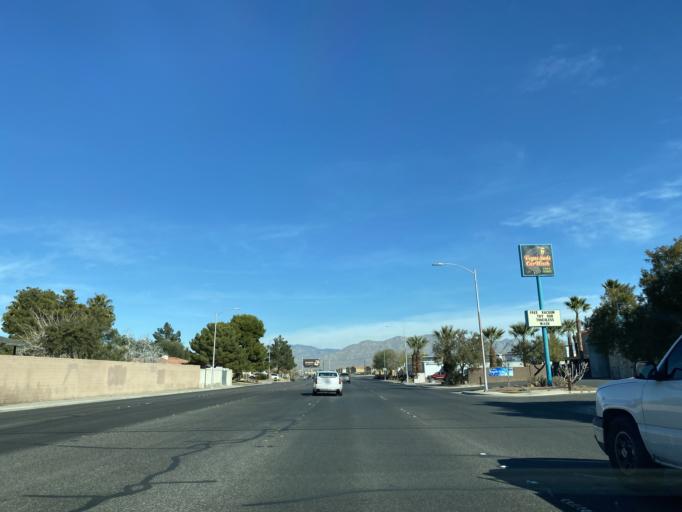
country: US
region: Nevada
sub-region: Clark County
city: Las Vegas
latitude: 36.2280
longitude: -115.2255
